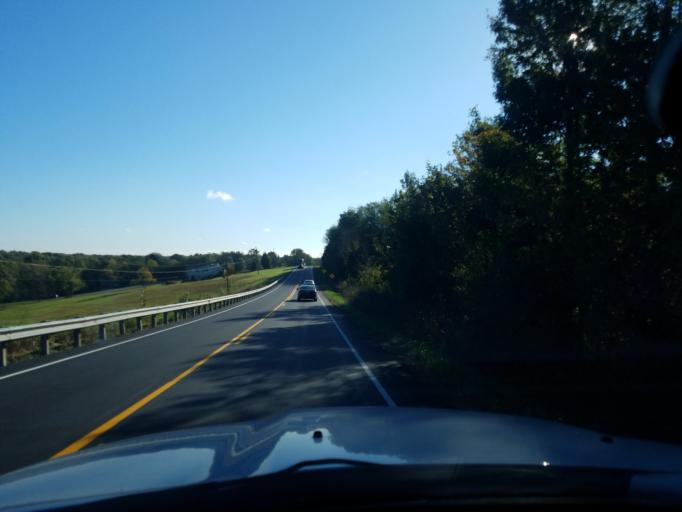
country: US
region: Kentucky
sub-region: Nelson County
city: Bardstown
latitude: 37.7761
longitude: -85.3683
